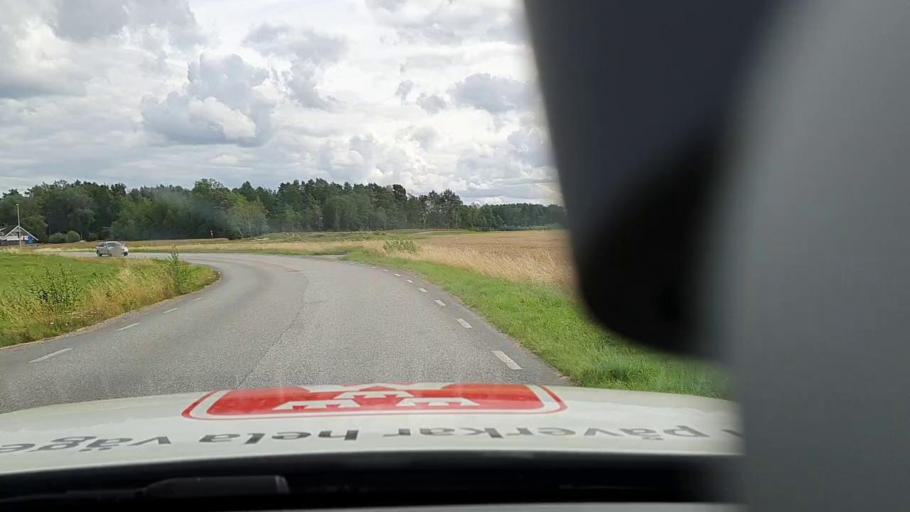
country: SE
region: Vaestra Goetaland
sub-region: Lidkopings Kommun
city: Lidkoping
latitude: 58.5565
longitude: 13.1150
